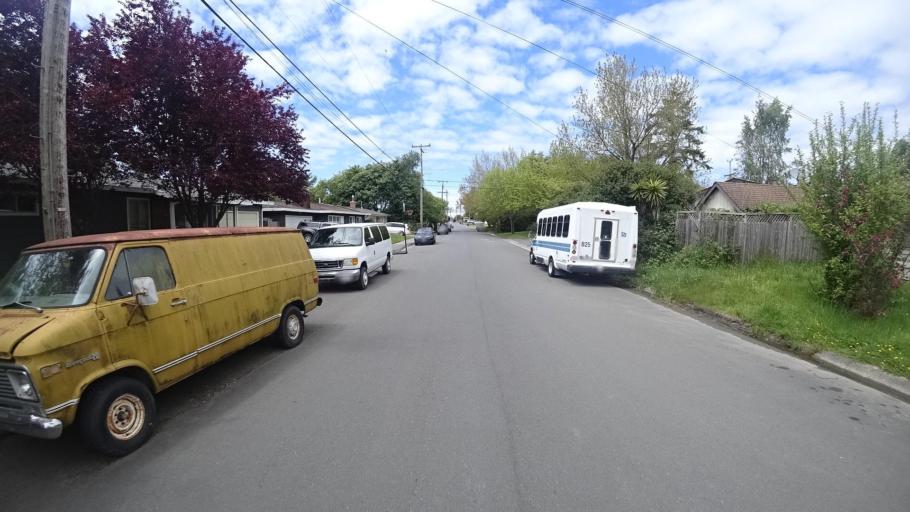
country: US
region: California
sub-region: Humboldt County
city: Arcata
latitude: 40.8839
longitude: -124.0879
